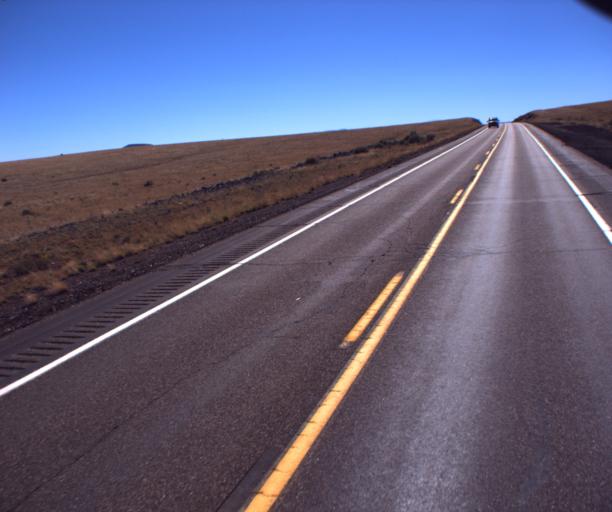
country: US
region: Arizona
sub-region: Apache County
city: Springerville
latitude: 34.3031
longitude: -109.3776
